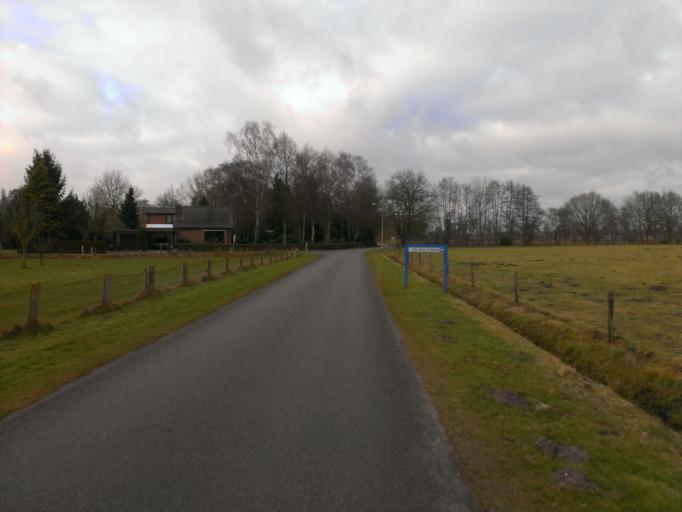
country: NL
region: Gelderland
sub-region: Gemeente Heerde
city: Heerde
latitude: 52.3666
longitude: 6.0281
